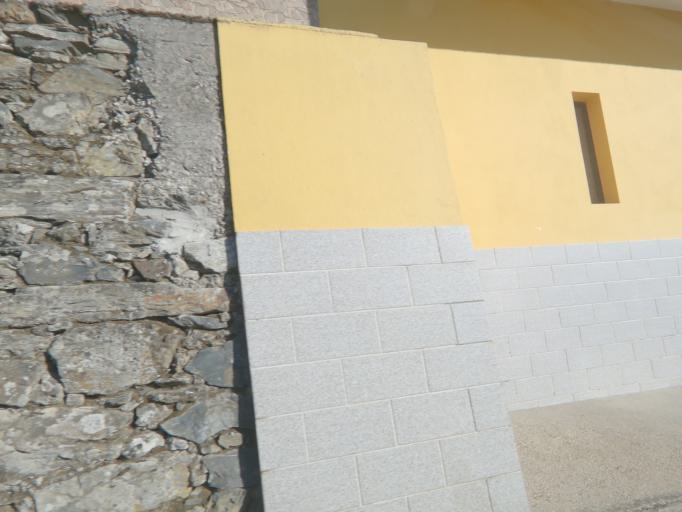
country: PT
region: Vila Real
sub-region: Peso da Regua
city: Peso da Regua
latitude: 41.1954
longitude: -7.7572
